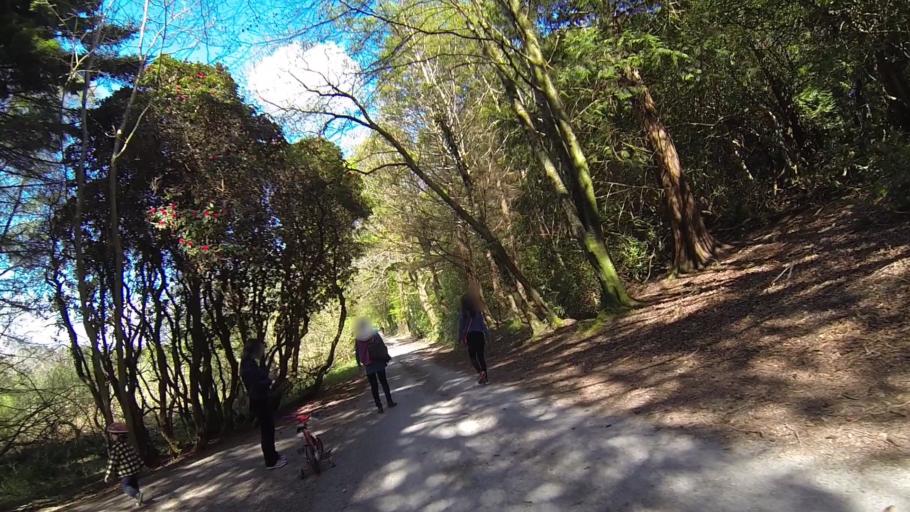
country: IE
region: Munster
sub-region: Ciarrai
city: Cill Airne
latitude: 52.0141
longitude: -9.5071
